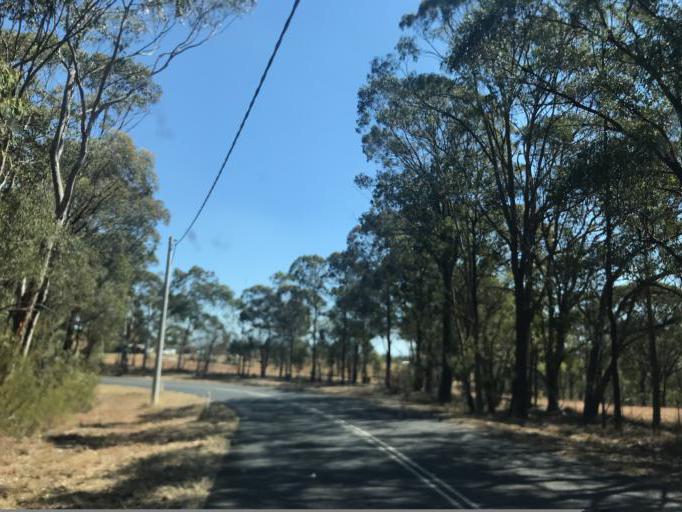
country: AU
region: New South Wales
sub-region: Hawkesbury
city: Pitt Town
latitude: -33.4615
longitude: 150.8516
